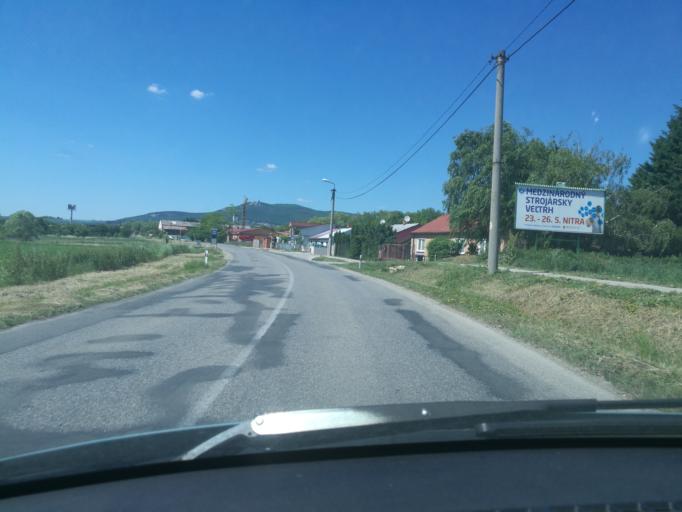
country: SK
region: Nitriansky
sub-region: Okres Nitra
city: Nitra
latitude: 48.2948
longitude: 18.1283
